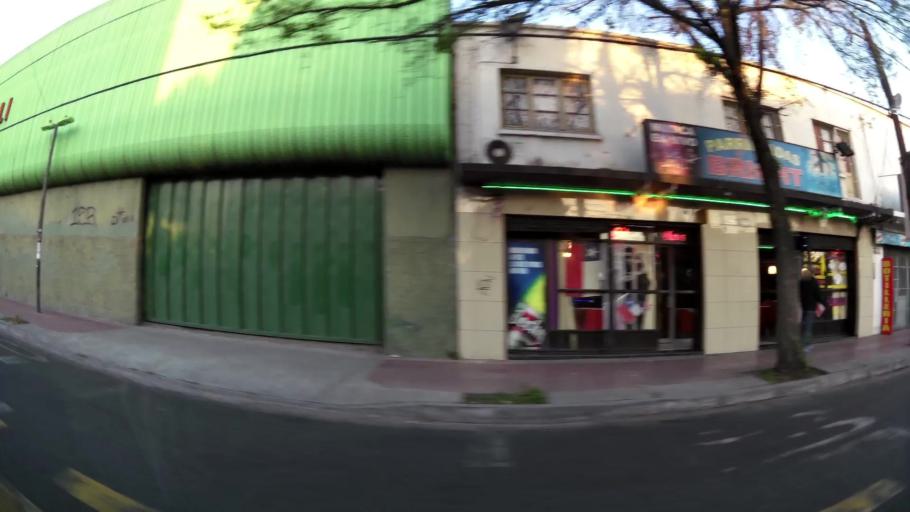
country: CL
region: Santiago Metropolitan
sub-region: Provincia de Santiago
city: La Pintana
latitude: -33.5296
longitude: -70.6622
